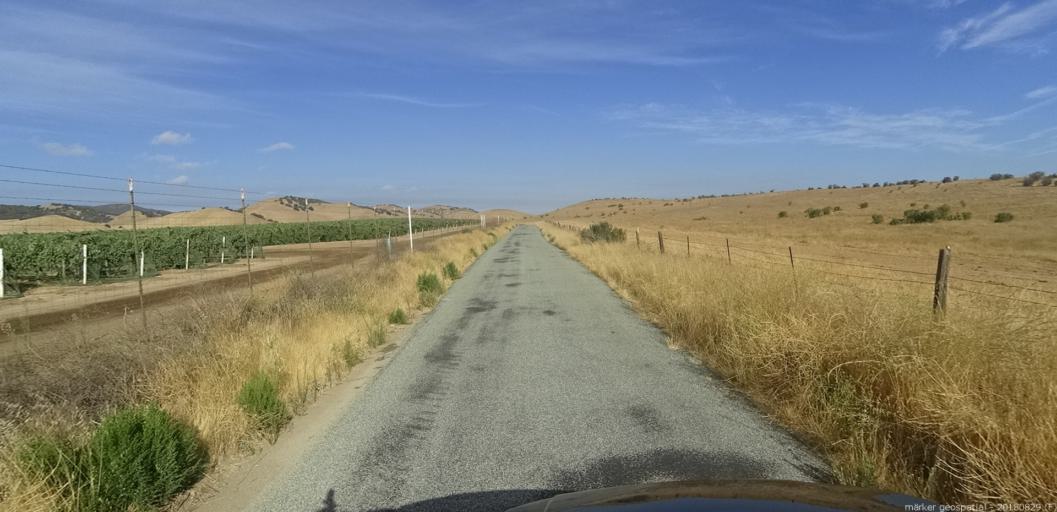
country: US
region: California
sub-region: Monterey County
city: King City
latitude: 36.0169
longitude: -120.9414
